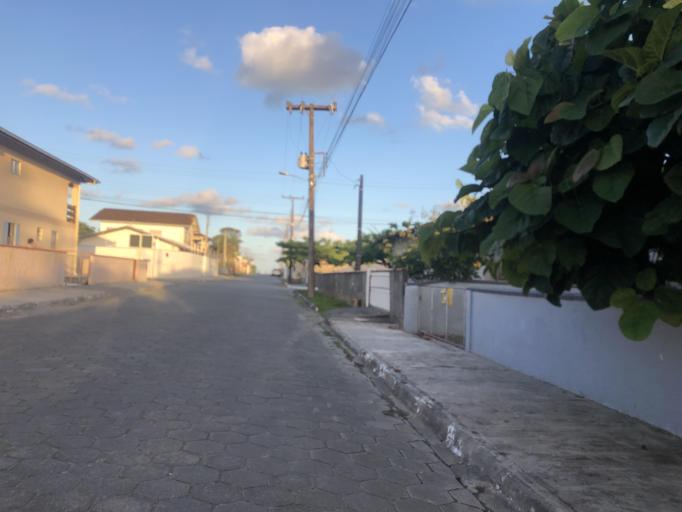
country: BR
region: Santa Catarina
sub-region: Sao Francisco Do Sul
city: Sao Francisco do Sul
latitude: -26.2194
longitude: -48.5256
